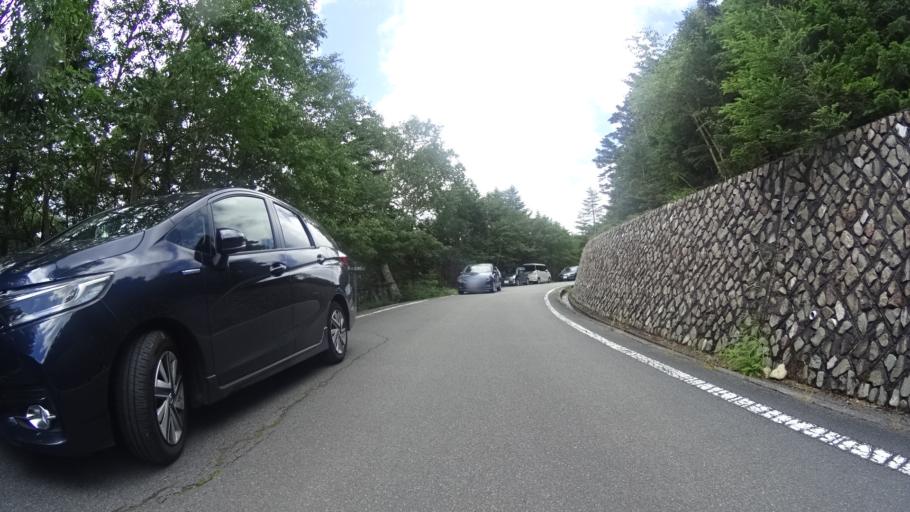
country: JP
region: Yamanashi
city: Enzan
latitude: 35.8712
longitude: 138.6629
